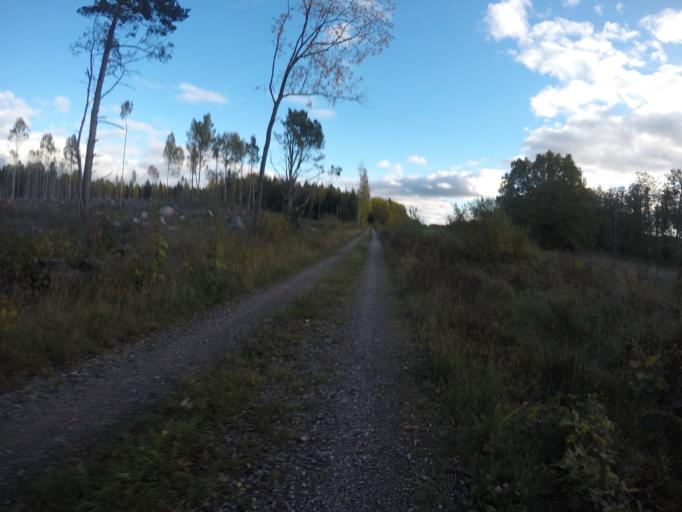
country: SE
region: Vaestmanland
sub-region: Arboga Kommun
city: Tyringe
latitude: 59.3191
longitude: 15.9761
